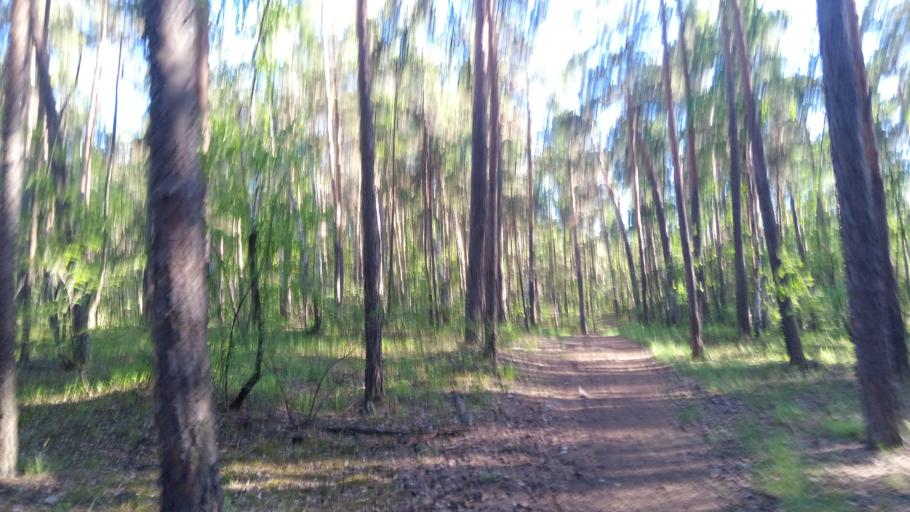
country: RU
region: Chelyabinsk
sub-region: Gorod Chelyabinsk
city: Chelyabinsk
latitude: 55.1331
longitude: 61.3362
